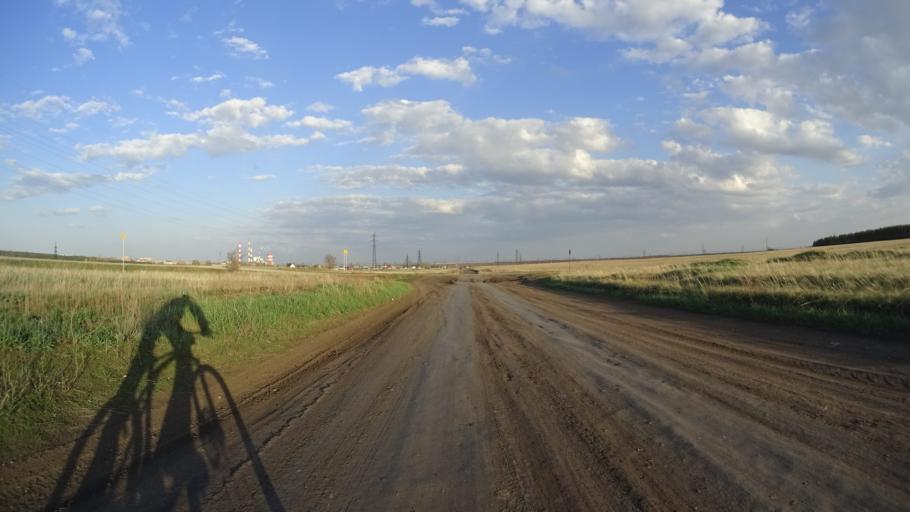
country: RU
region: Chelyabinsk
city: Troitsk
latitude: 54.0501
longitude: 61.5944
